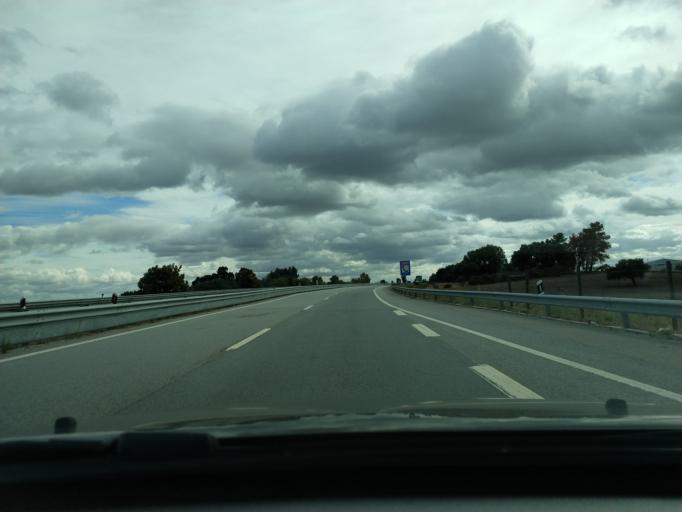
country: PT
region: Guarda
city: Alcains
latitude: 40.0239
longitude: -7.4660
